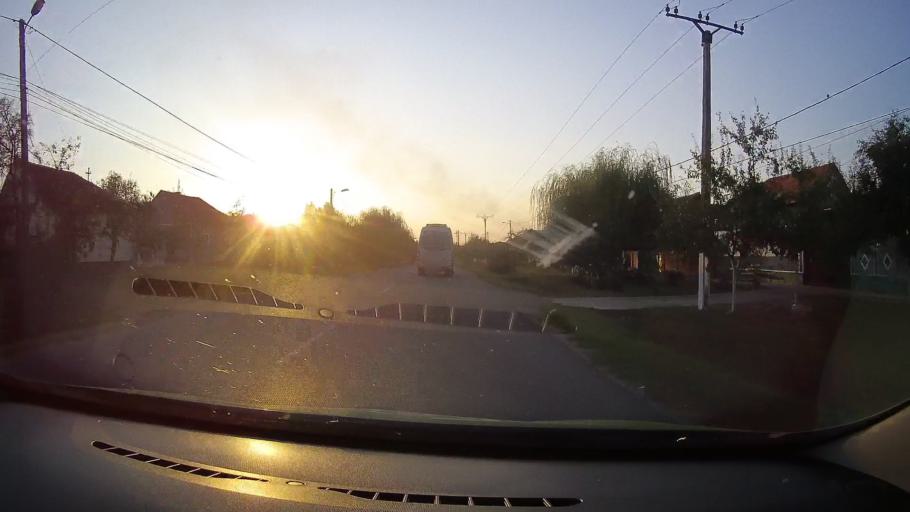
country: RO
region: Arad
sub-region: Comuna Sicula
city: Sicula
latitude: 46.4368
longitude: 21.7621
